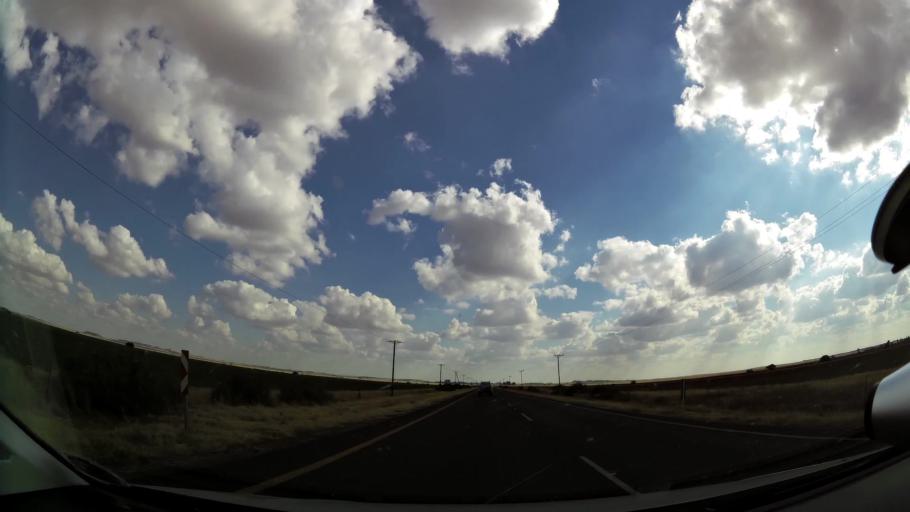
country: ZA
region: Orange Free State
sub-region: Xhariep District Municipality
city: Koffiefontein
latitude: -29.1308
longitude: 25.5228
